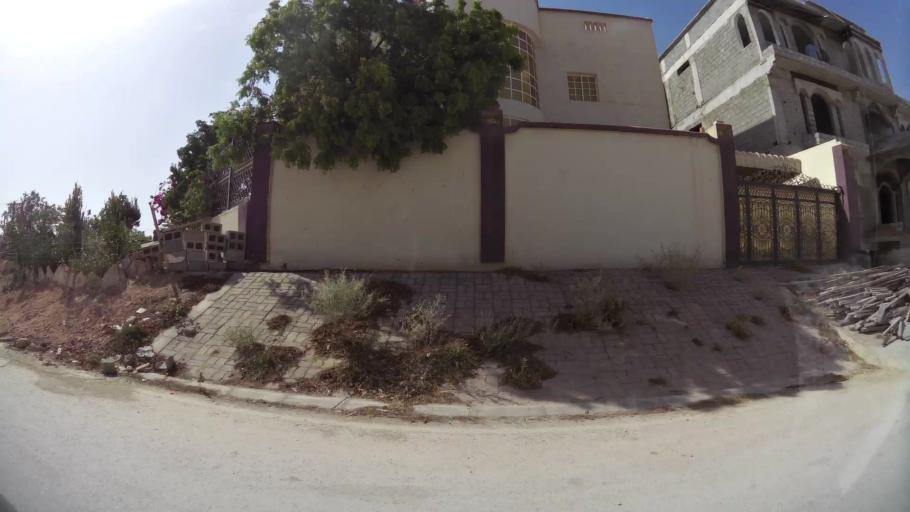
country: OM
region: Zufar
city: Salalah
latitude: 16.9991
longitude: 54.0190
